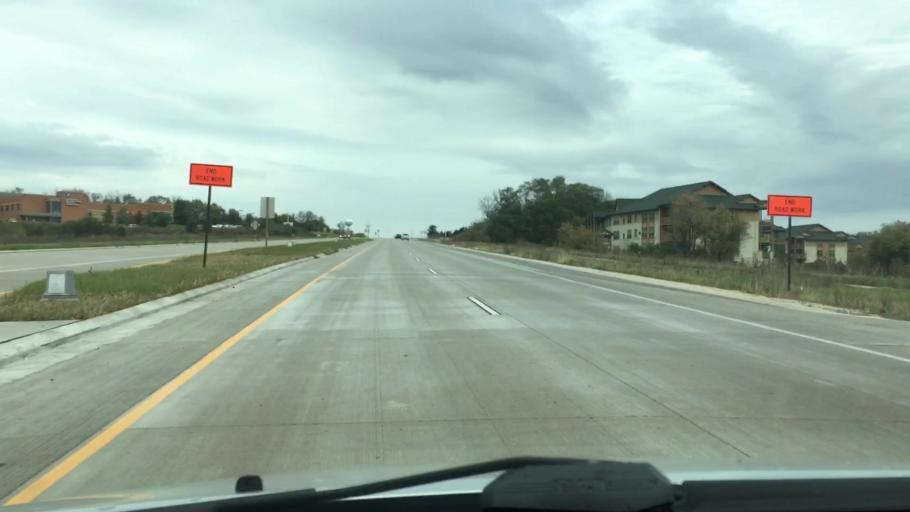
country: US
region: Wisconsin
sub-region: Waukesha County
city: Waukesha
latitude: 43.0235
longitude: -88.2858
